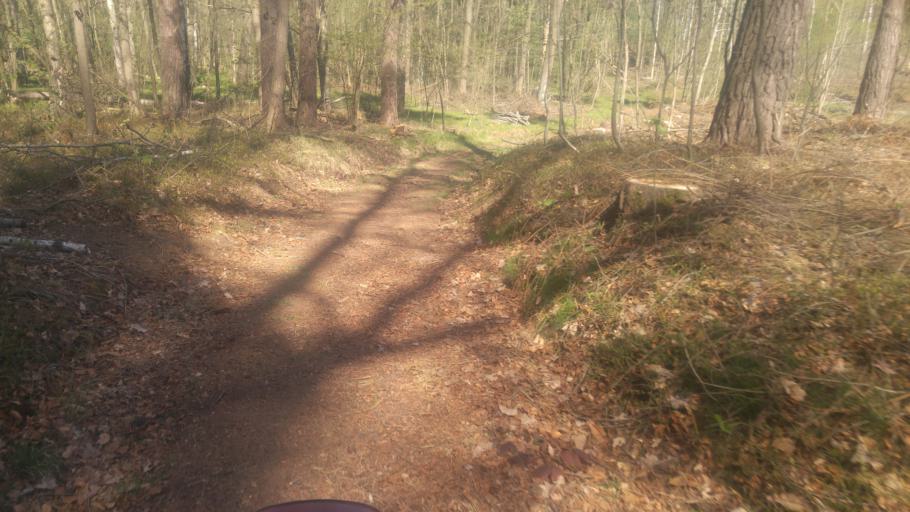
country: DE
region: Saxony
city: Altmittweida
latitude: 50.9516
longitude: 12.9604
